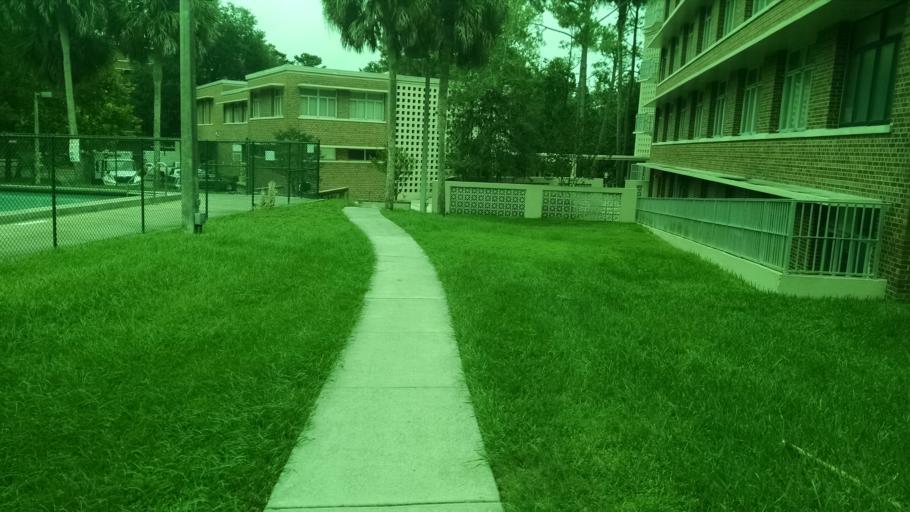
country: US
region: Florida
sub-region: Alachua County
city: Gainesville
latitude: 29.6460
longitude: -82.3519
